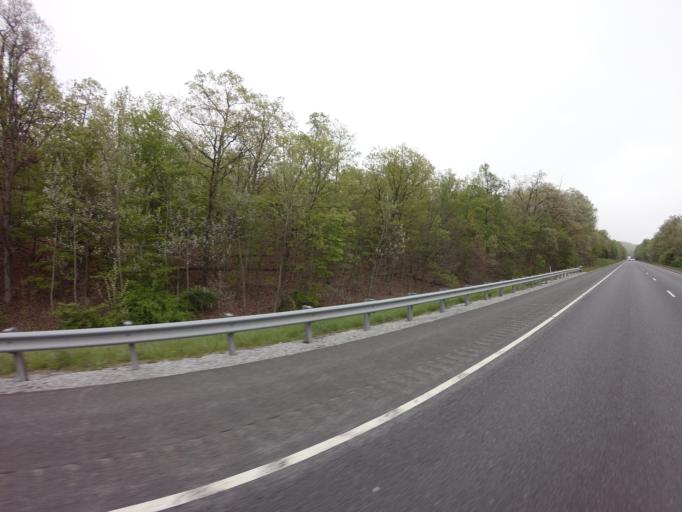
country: US
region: Maryland
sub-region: Washington County
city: Boonsboro
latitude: 39.5635
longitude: -77.6157
